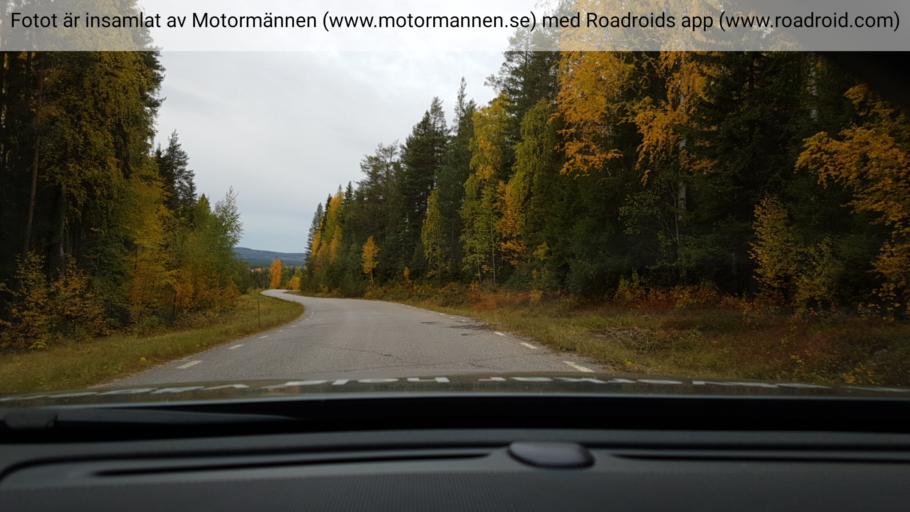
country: SE
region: Norrbotten
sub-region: Overkalix Kommun
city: OEverkalix
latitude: 66.2334
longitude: 22.9884
